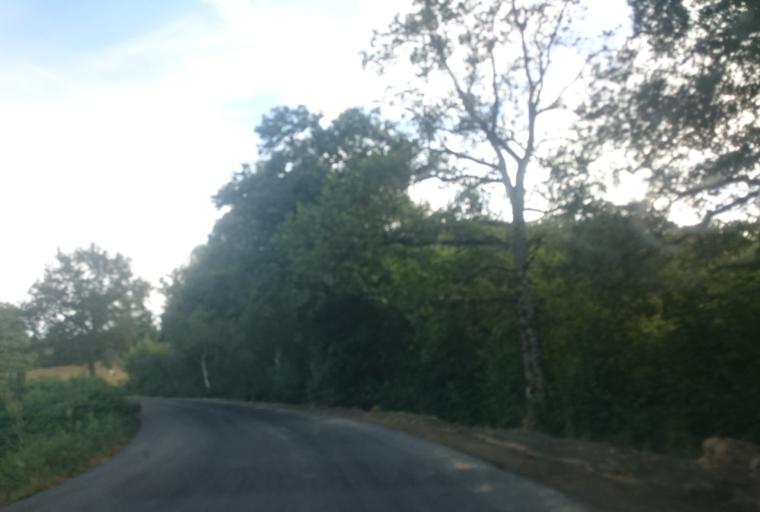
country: FR
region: Auvergne
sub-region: Departement du Cantal
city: Laroquebrou
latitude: 44.9292
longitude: 2.1933
